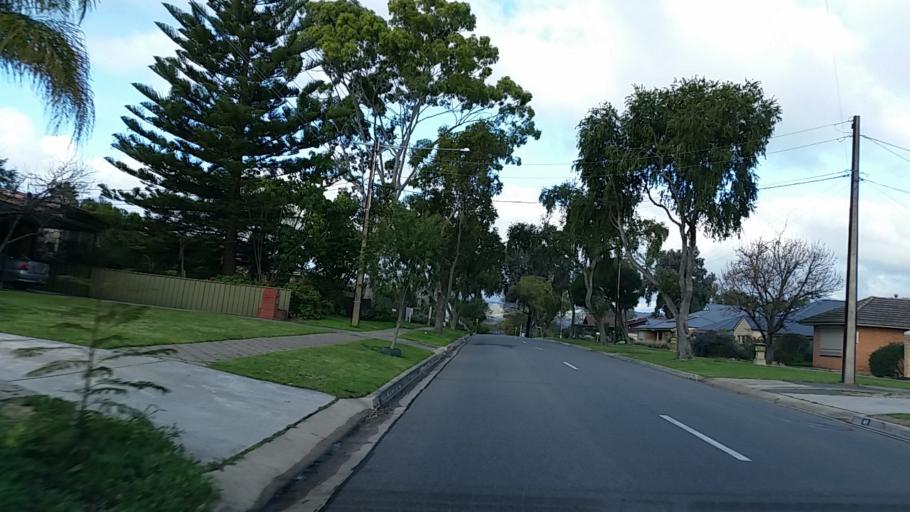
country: AU
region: South Australia
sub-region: Tea Tree Gully
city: Modbury
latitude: -34.8378
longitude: 138.6669
